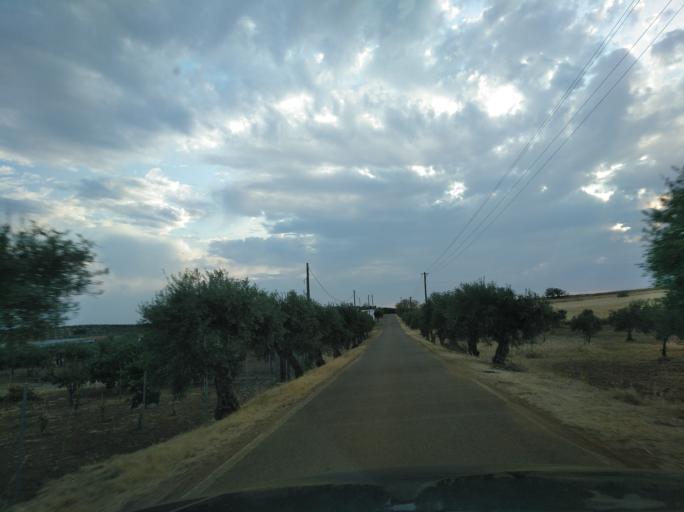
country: PT
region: Portalegre
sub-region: Campo Maior
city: Campo Maior
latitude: 39.0165
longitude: -7.0311
